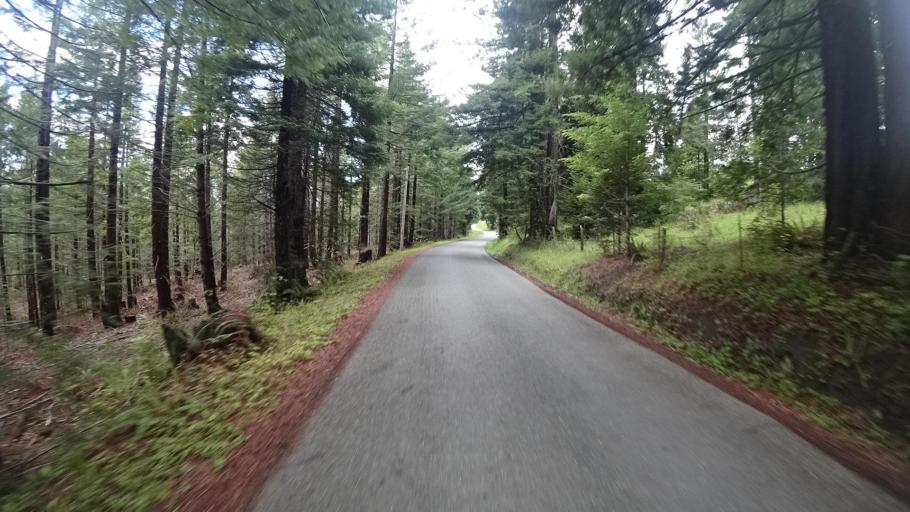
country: US
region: California
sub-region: Humboldt County
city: Blue Lake
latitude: 40.8564
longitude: -123.9319
